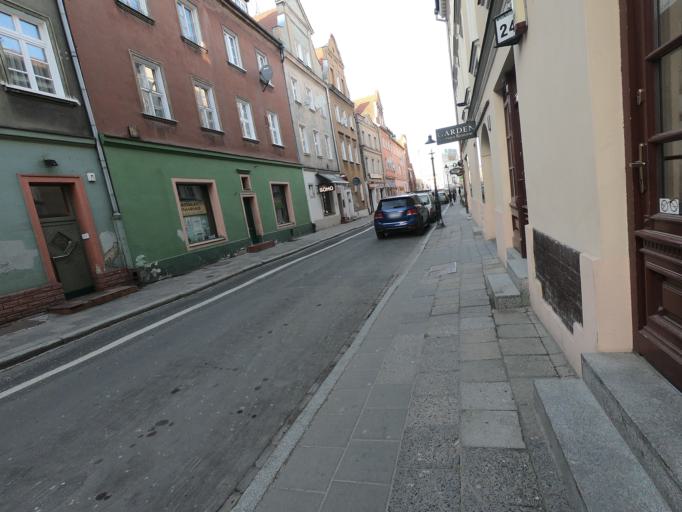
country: PL
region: Greater Poland Voivodeship
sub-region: Poznan
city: Poznan
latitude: 52.4093
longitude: 16.9339
